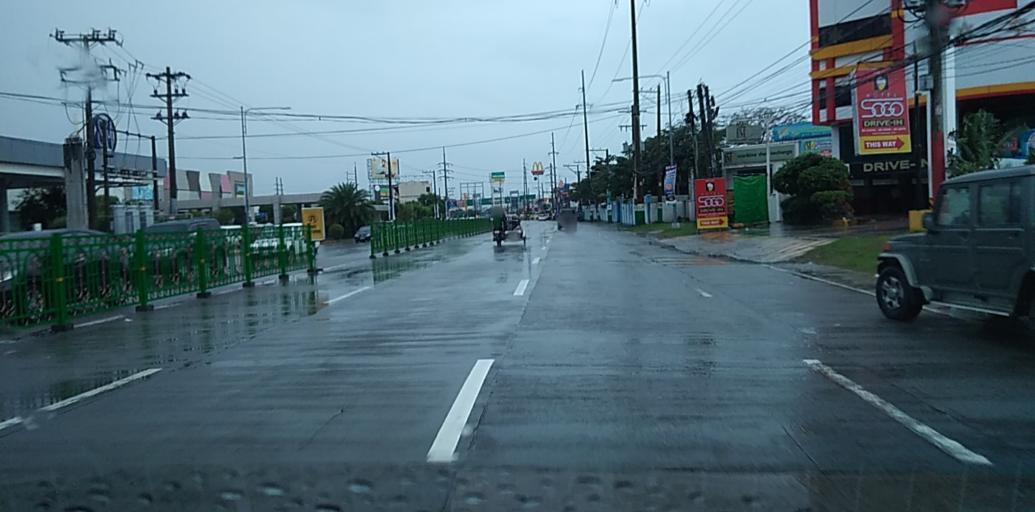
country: PH
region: Central Luzon
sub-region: Province of Pampanga
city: Del Pilar
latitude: 15.0513
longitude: 120.7008
